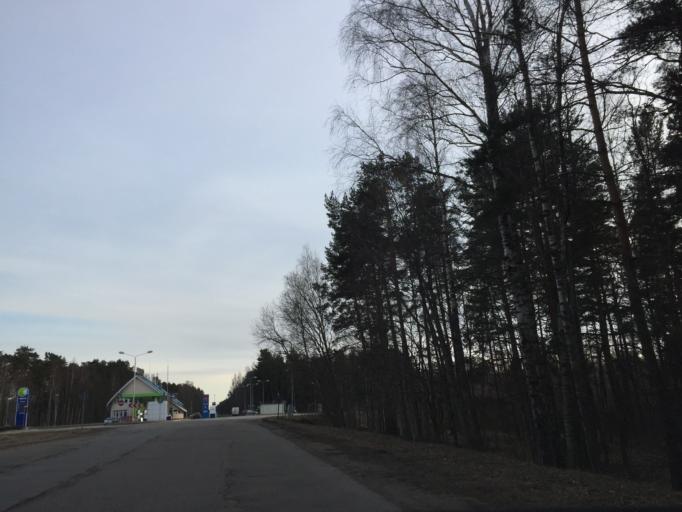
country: LV
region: Salacgrivas
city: Ainazi
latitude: 57.8510
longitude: 24.3540
